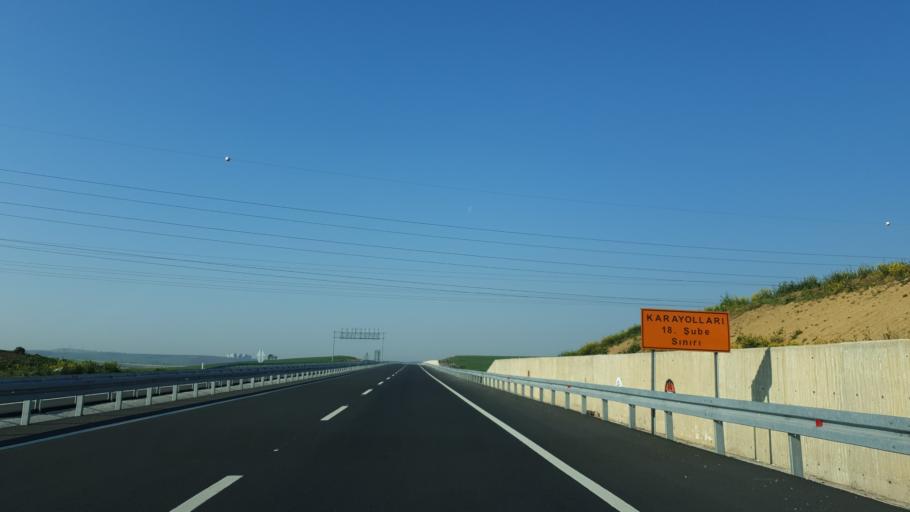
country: TR
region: Tekirdag
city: Marmaracik
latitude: 41.1978
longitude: 27.7545
